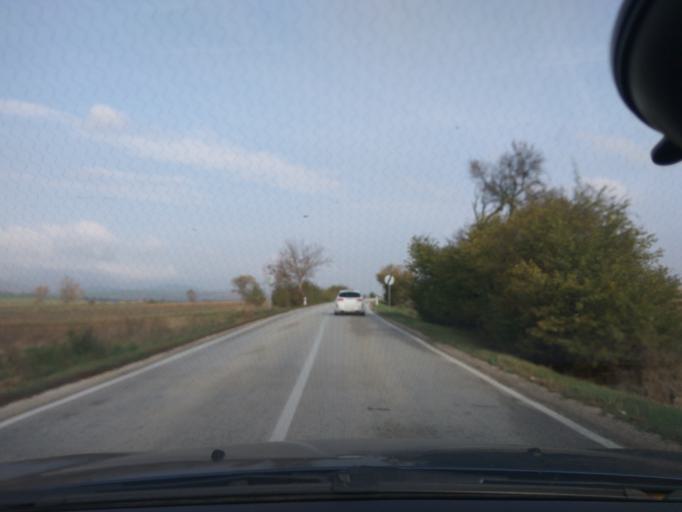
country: SK
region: Nitriansky
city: Cachtice
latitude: 48.6619
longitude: 17.7608
